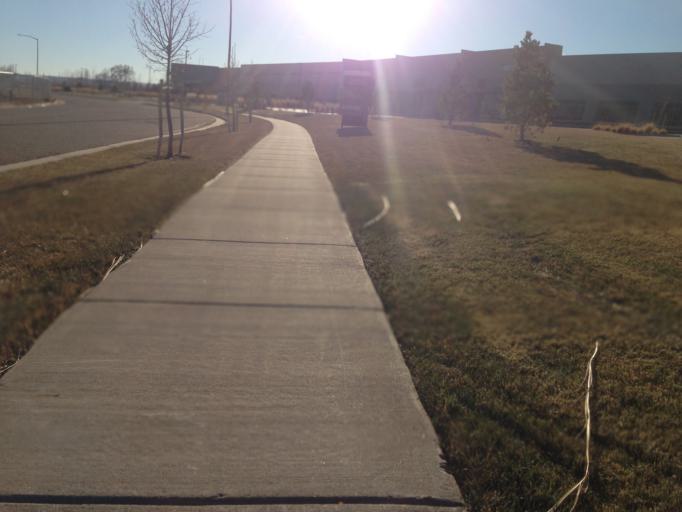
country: US
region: Colorado
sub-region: Boulder County
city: Louisville
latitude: 39.9620
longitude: -105.1124
